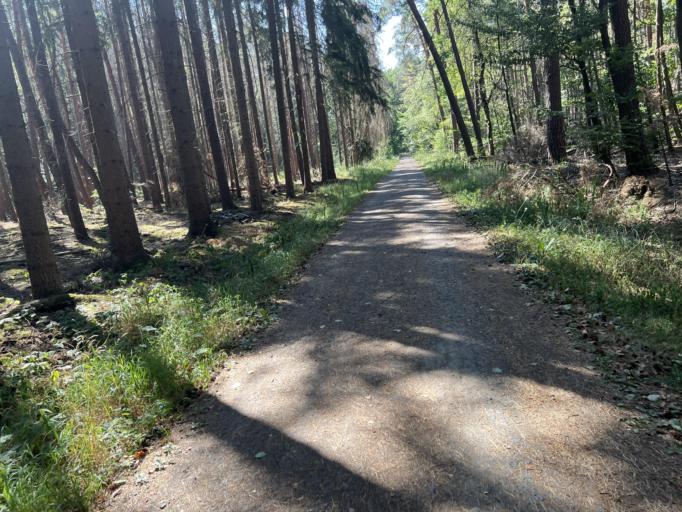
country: DE
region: Hesse
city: Obertshausen
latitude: 50.0783
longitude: 8.8326
